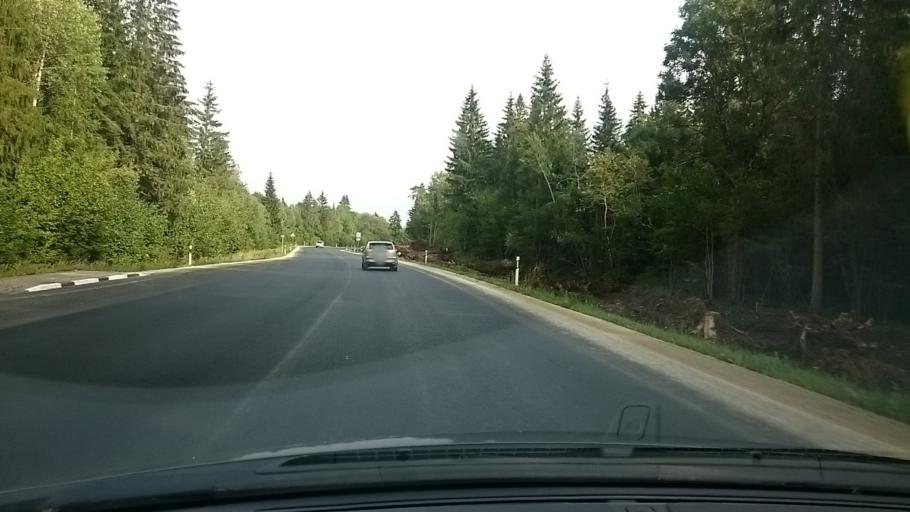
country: EE
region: Harju
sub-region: Saku vald
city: Saku
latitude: 59.3022
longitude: 24.6399
